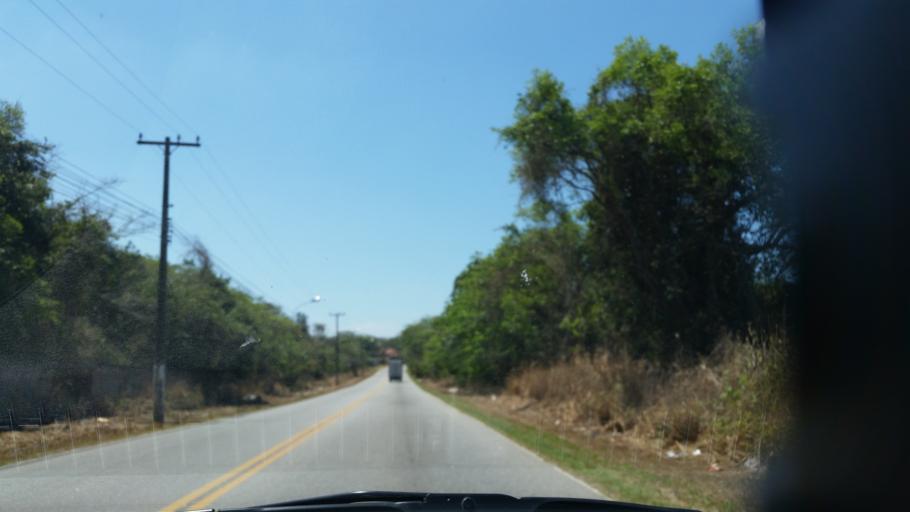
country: BR
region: Rio de Janeiro
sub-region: Cabo Frio
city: Cabo Frio
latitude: -22.8511
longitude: -42.0034
